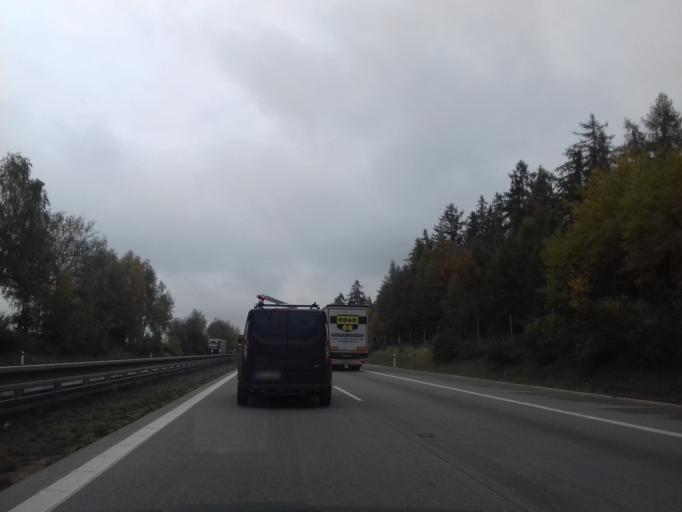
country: CZ
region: Central Bohemia
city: Cechtice
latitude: 49.6318
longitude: 15.1292
